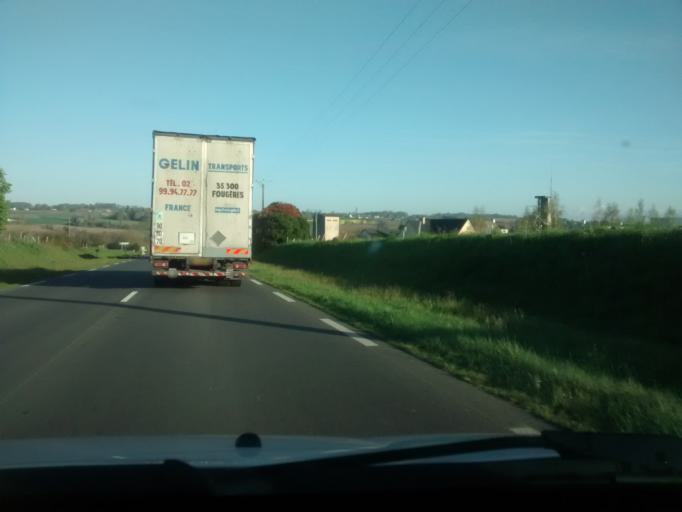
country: FR
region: Brittany
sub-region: Departement d'Ille-et-Vilaine
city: Antrain
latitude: 48.4535
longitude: -1.4834
